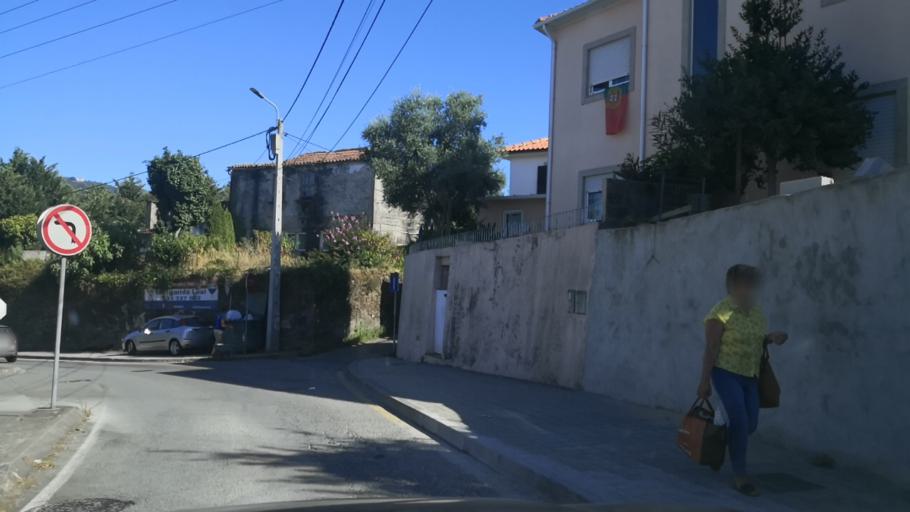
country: PT
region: Porto
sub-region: Santo Tirso
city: Santo Tirso
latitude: 41.3387
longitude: -8.4842
